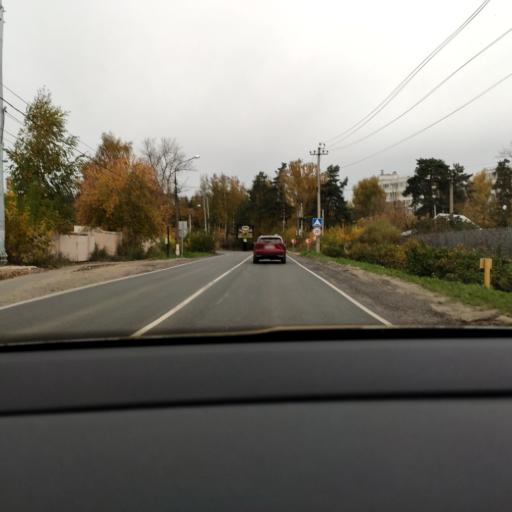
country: RU
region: Moskovskaya
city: Ivanteyevka
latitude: 55.9852
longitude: 37.9308
